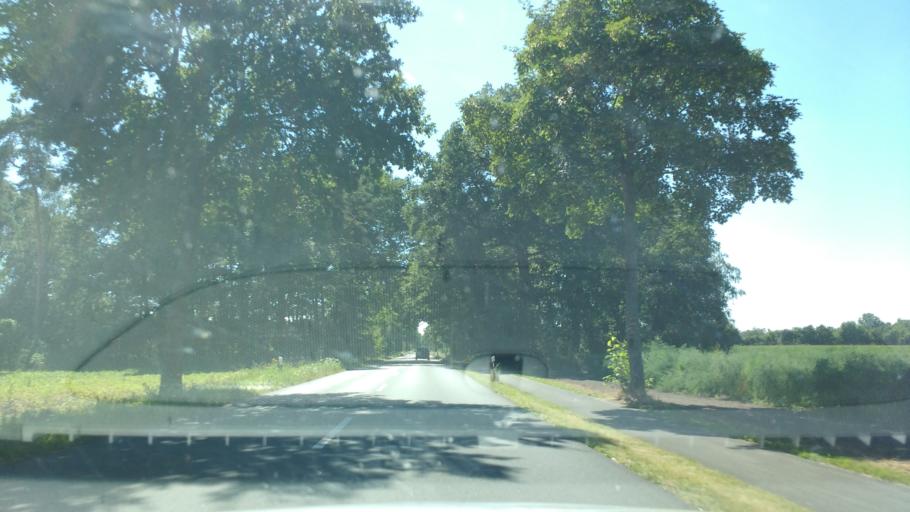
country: DE
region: North Rhine-Westphalia
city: Rietberg
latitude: 51.7244
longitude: 8.4624
